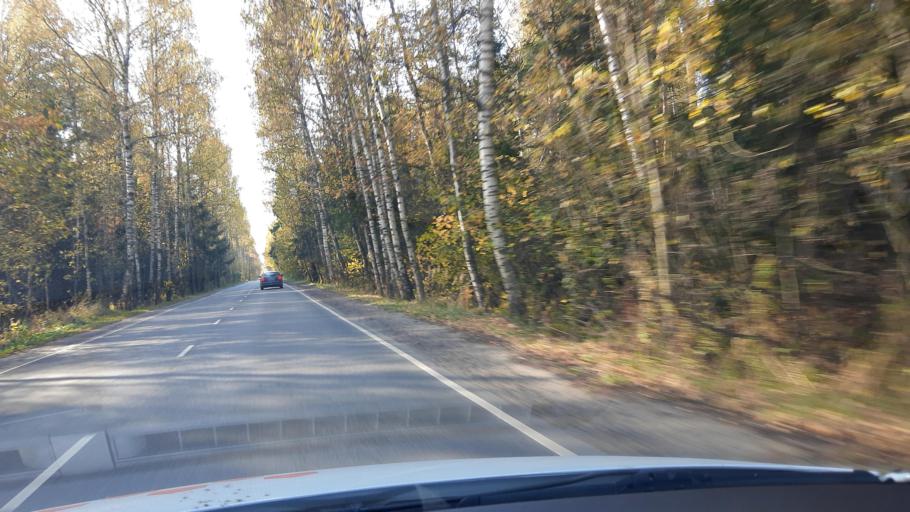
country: RU
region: Moskovskaya
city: Elektrostal'
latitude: 55.8014
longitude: 38.3967
